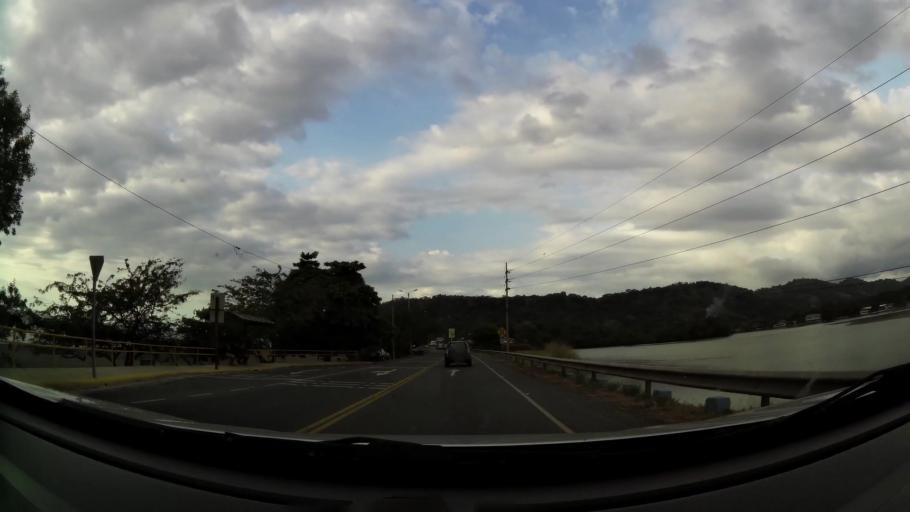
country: CR
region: Puntarenas
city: Esparza
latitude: 9.9204
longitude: -84.7128
